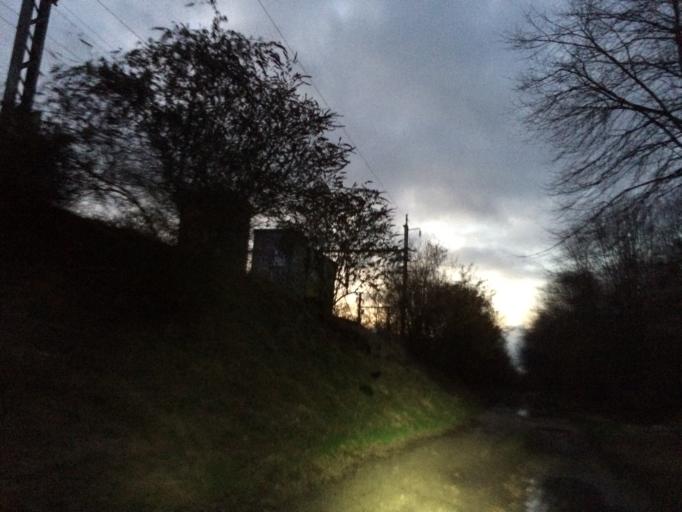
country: FR
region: Picardie
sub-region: Departement de l'Oise
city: Coye-la-Foret
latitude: 49.1422
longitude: 2.4871
